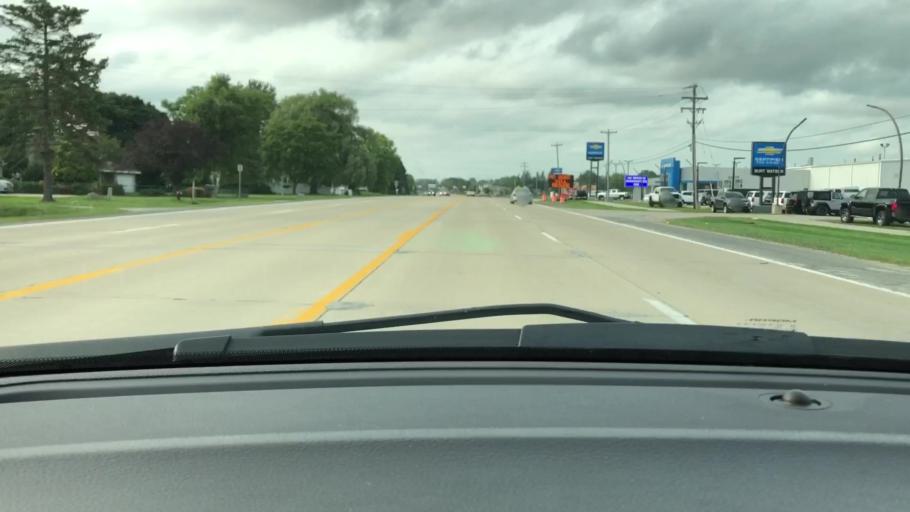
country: US
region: Michigan
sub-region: Saginaw County
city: Freeland
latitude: 43.5152
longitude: -84.1191
